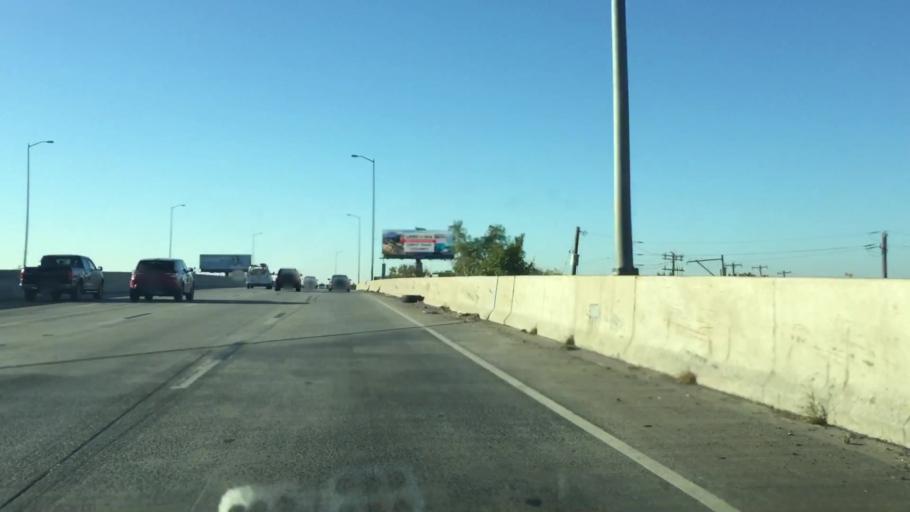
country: US
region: New Jersey
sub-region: Burlington County
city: Riverton
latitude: 40.0318
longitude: -75.0215
